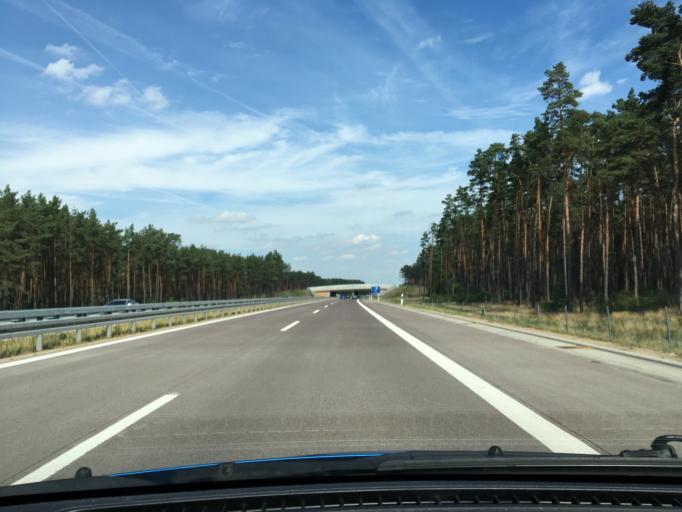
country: DE
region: Mecklenburg-Vorpommern
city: Gross Laasch
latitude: 53.3662
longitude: 11.5167
